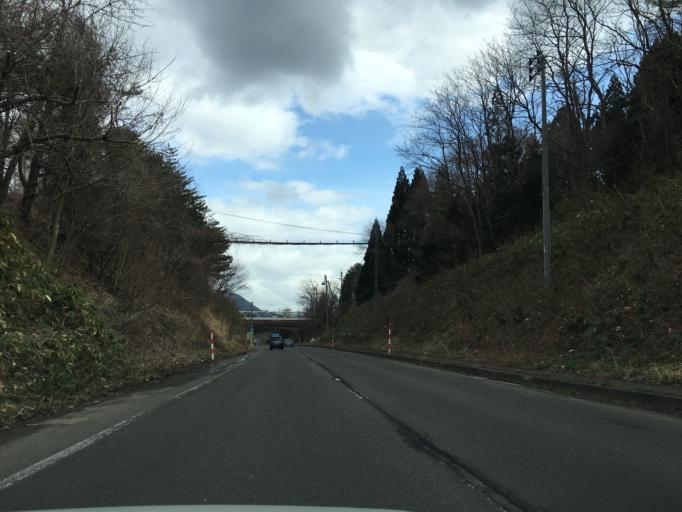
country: JP
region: Akita
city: Odate
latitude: 40.2184
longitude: 140.6422
